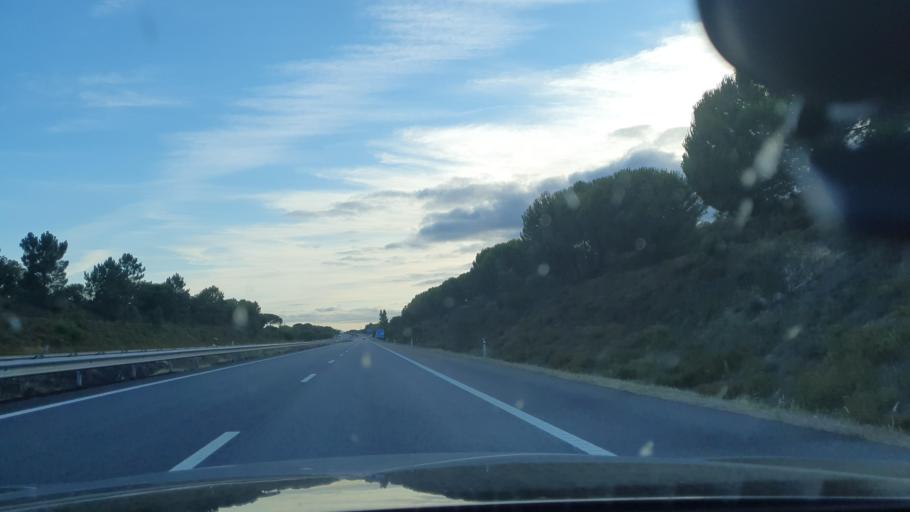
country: PT
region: Evora
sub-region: Vendas Novas
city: Vendas Novas
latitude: 38.6244
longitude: -8.5651
